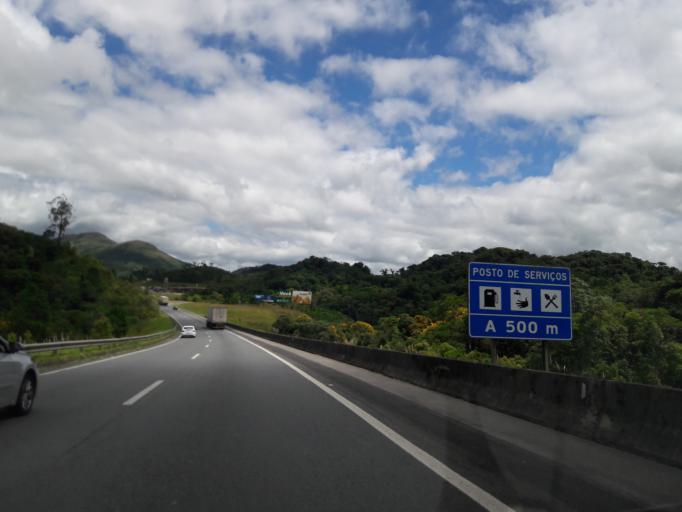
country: BR
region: Parana
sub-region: Antonina
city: Antonina
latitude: -25.1069
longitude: -48.7858
